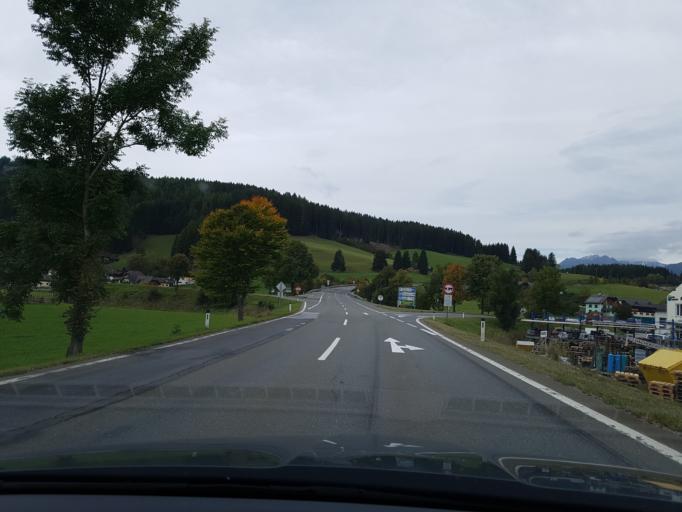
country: AT
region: Salzburg
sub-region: Politischer Bezirk Tamsweg
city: Tamsweg
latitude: 47.1316
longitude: 13.7936
